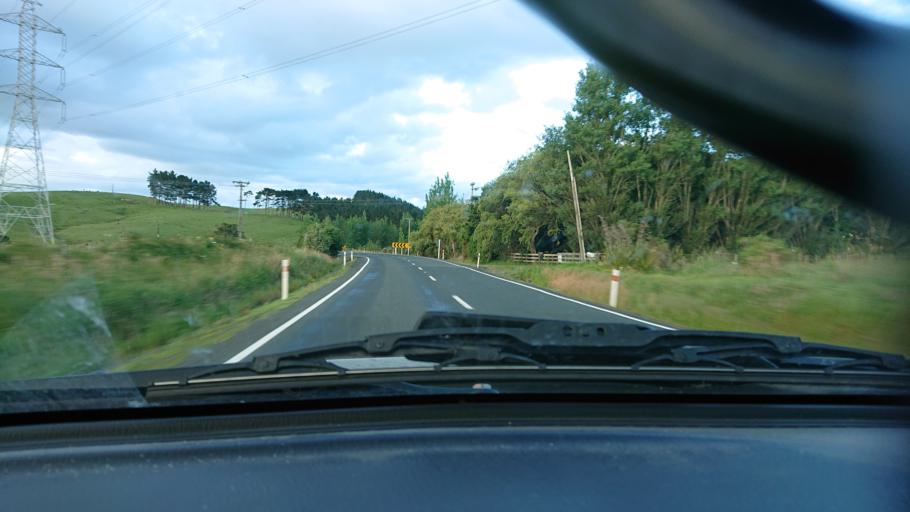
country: NZ
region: Auckland
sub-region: Auckland
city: Parakai
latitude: -36.4837
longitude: 174.4503
